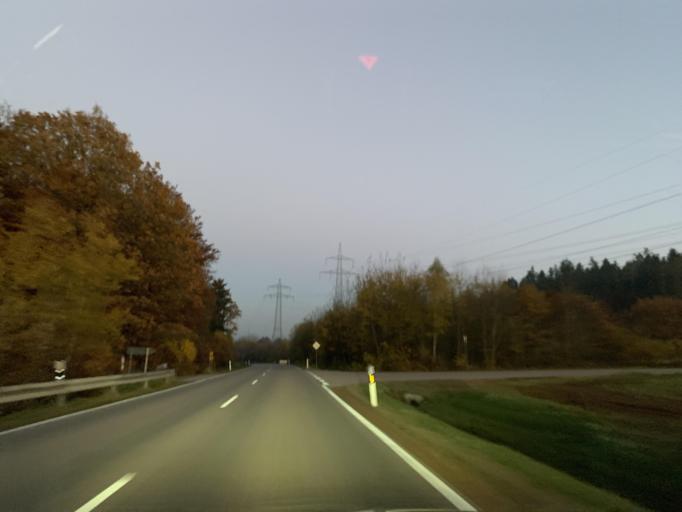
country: DE
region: Bavaria
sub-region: Upper Palatinate
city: Brunn
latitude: 49.2405
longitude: 12.2184
